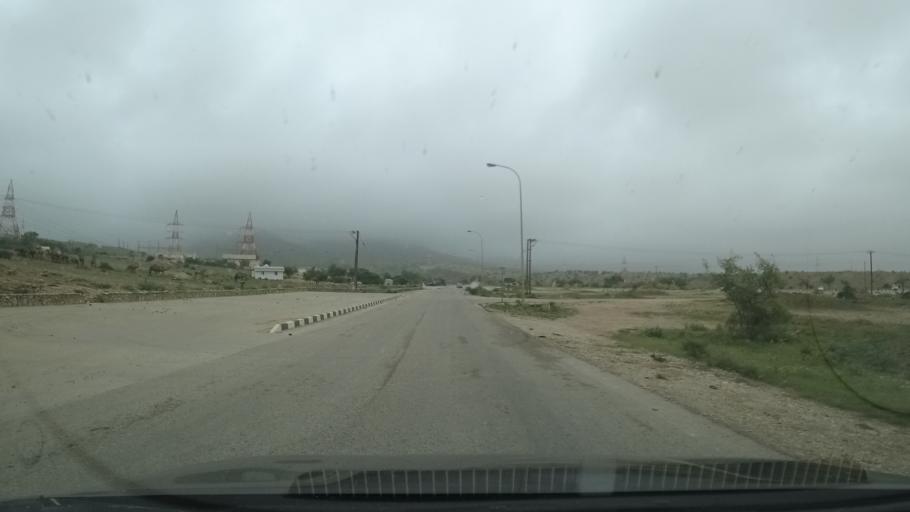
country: OM
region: Zufar
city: Salalah
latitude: 17.0884
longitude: 54.0779
